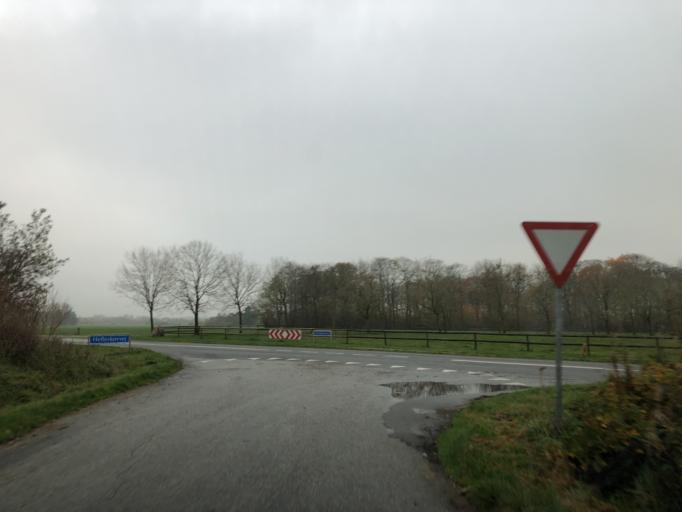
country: DK
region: Central Jutland
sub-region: Herning Kommune
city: Vildbjerg
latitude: 56.2081
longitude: 8.7570
